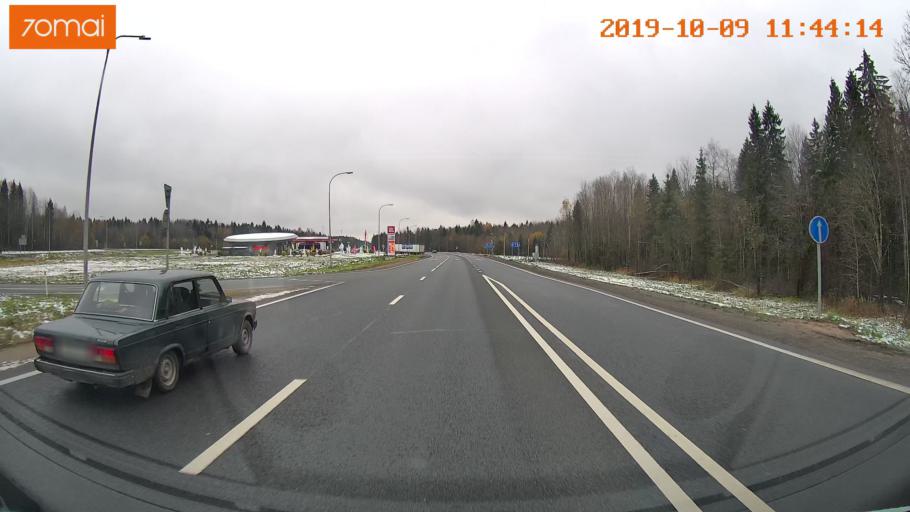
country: RU
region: Vologda
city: Gryazovets
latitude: 58.8858
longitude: 40.1900
